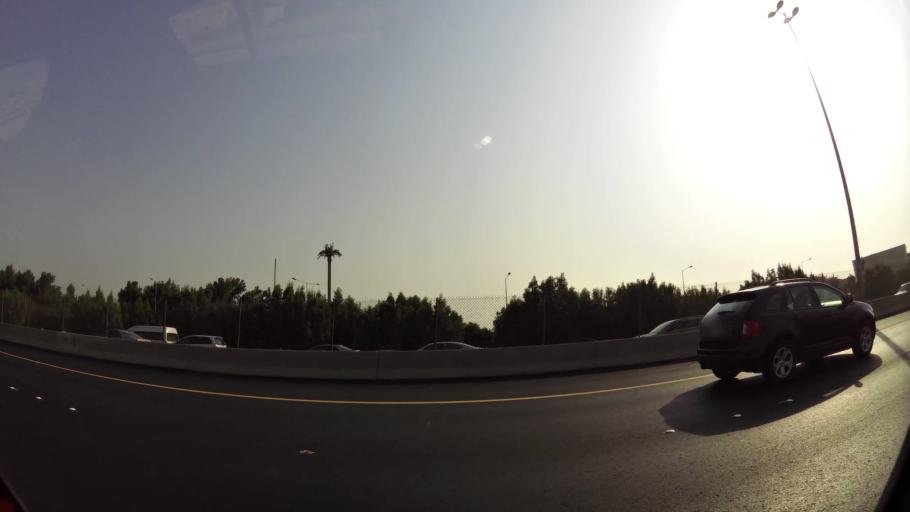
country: KW
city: Al Funaytis
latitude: 29.2177
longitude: 48.1017
